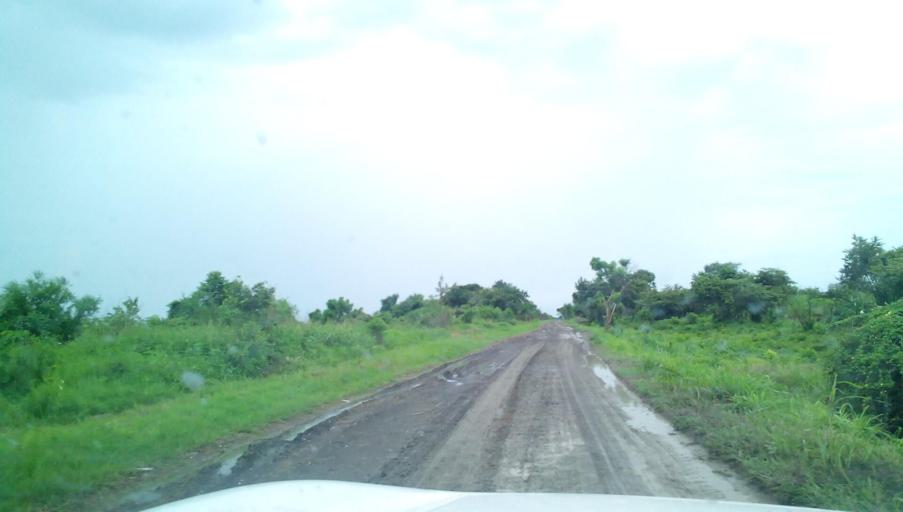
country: MX
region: Veracruz
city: Panuco
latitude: 21.8147
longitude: -98.1112
